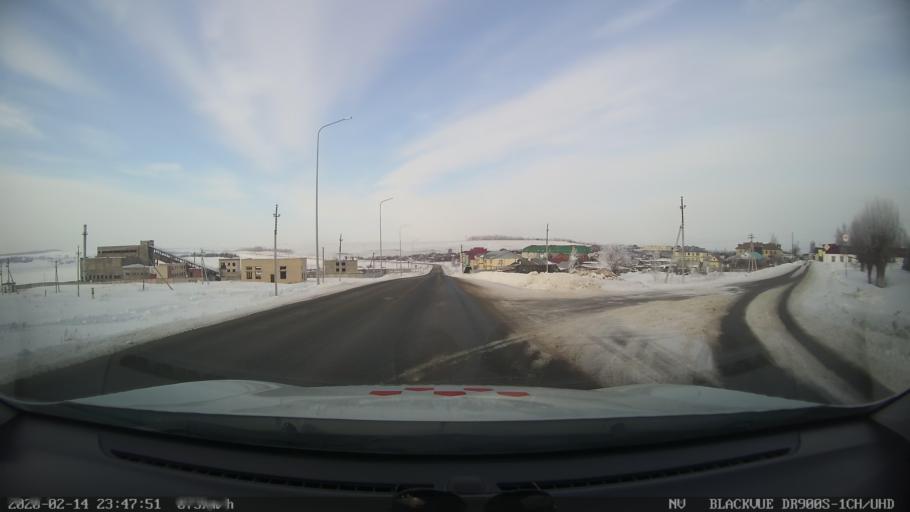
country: RU
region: Tatarstan
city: Kuybyshevskiy Zaton
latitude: 55.2435
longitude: 49.2066
